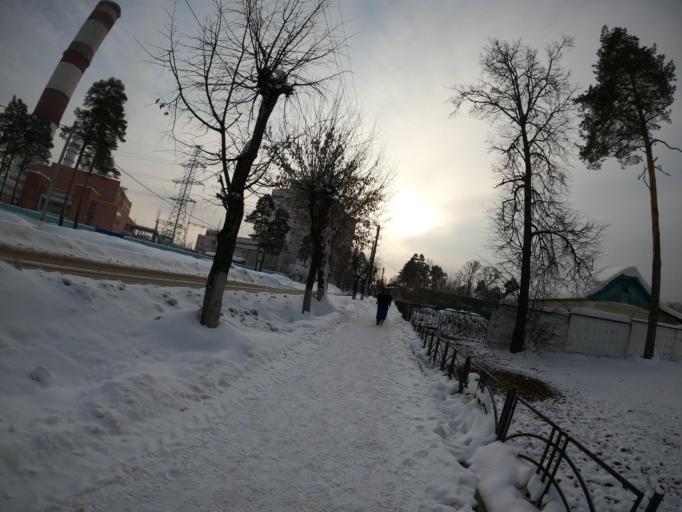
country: RU
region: Moskovskaya
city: Elektrogorsk
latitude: 55.8887
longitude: 38.7792
